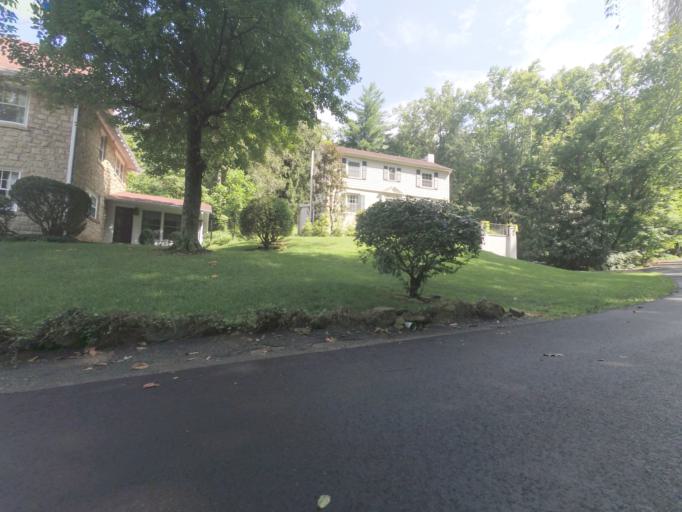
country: US
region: West Virginia
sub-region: Cabell County
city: Huntington
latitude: 38.4048
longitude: -82.4585
